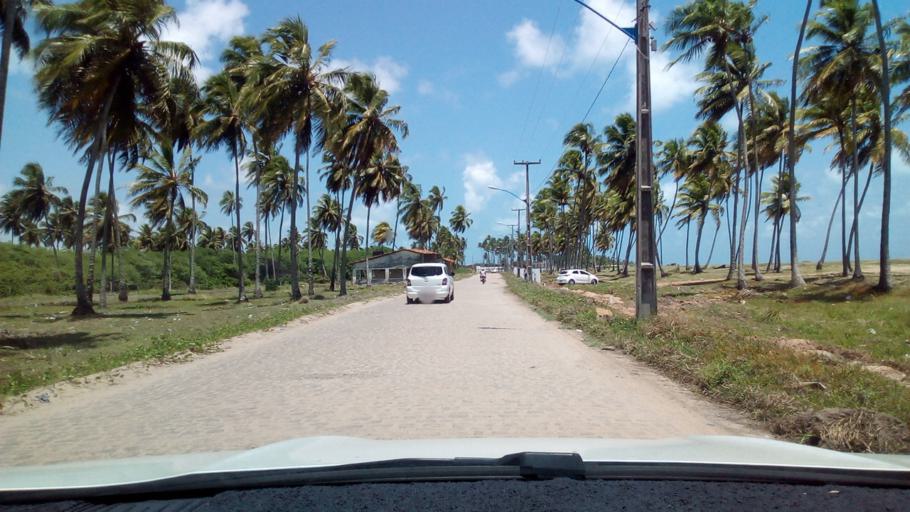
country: BR
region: Paraiba
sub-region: Pitimbu
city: Pitimbu
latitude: -7.5318
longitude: -34.8219
